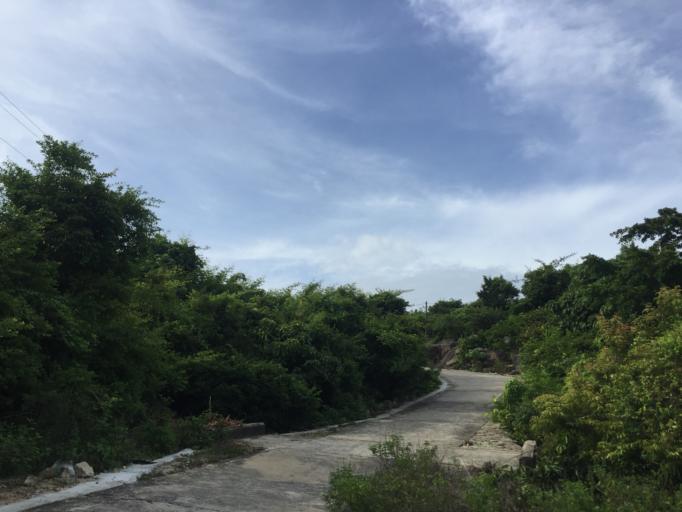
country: VN
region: Quang Nam
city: Hoi An
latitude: 15.9540
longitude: 108.5085
